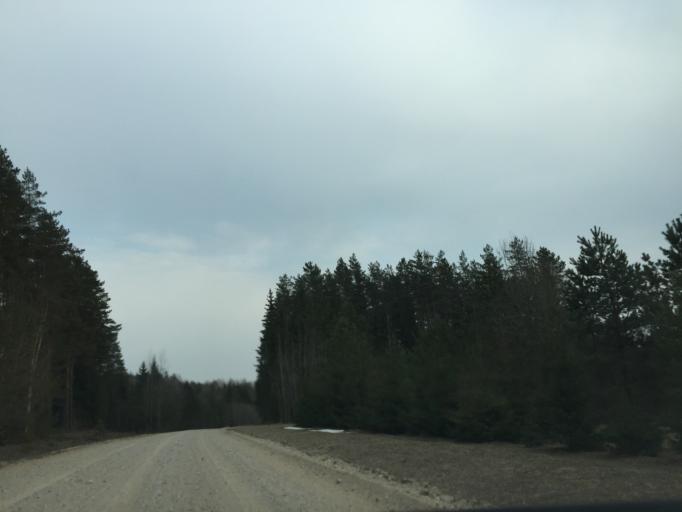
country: LV
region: Raunas
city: Rauna
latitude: 57.1636
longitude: 25.5187
